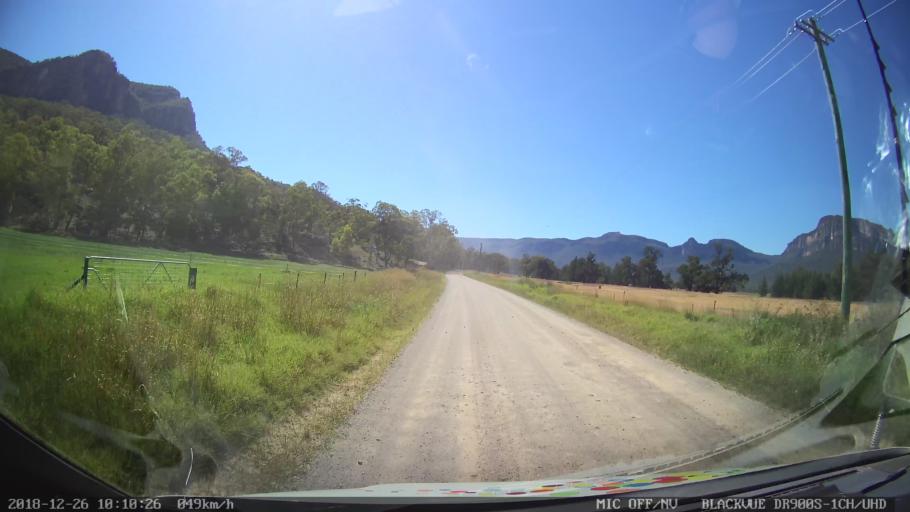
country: AU
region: New South Wales
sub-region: Lithgow
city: Portland
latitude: -33.1063
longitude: 150.2451
